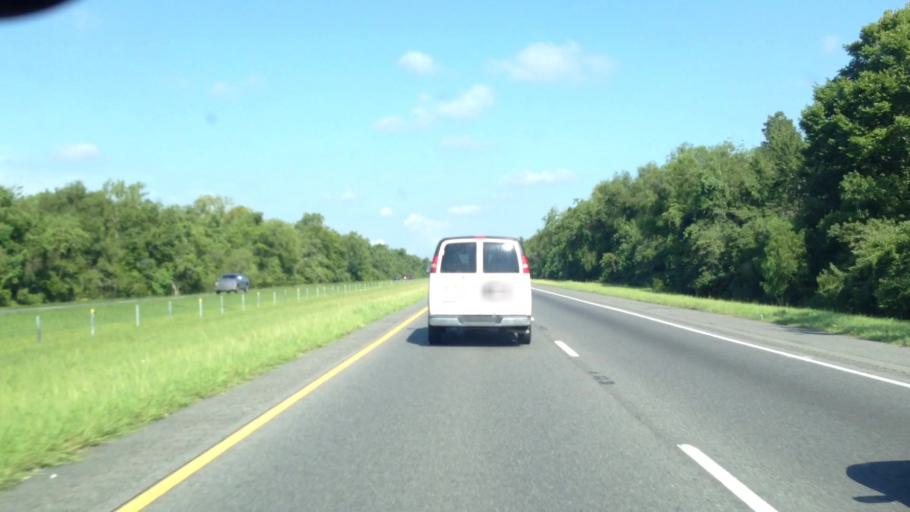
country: US
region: Louisiana
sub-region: Saint James Parish
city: Grand Point
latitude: 30.1351
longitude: -90.7308
